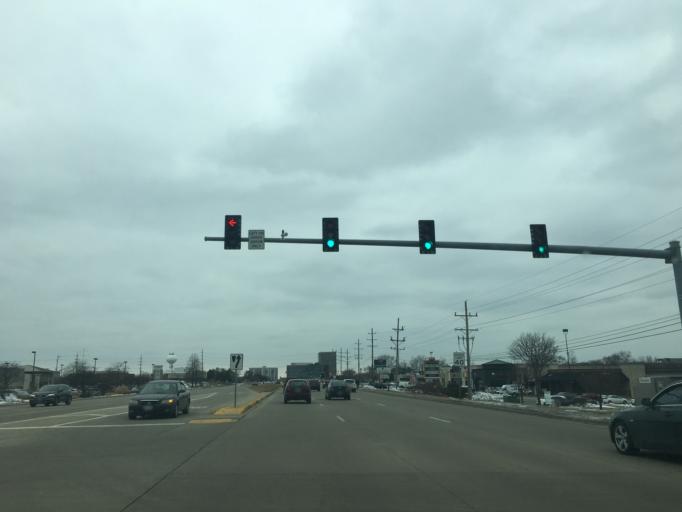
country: US
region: Illinois
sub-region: DuPage County
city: Oakbrook Terrace
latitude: 41.8464
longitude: -87.9679
